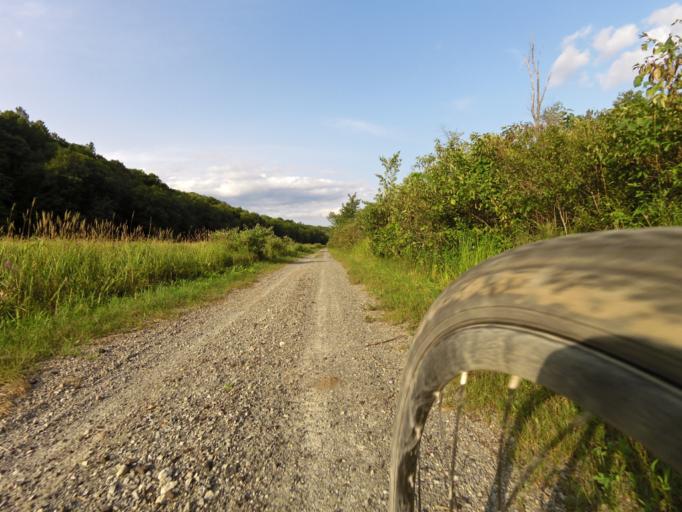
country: CA
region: Ontario
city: Kingston
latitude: 44.5044
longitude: -76.4350
